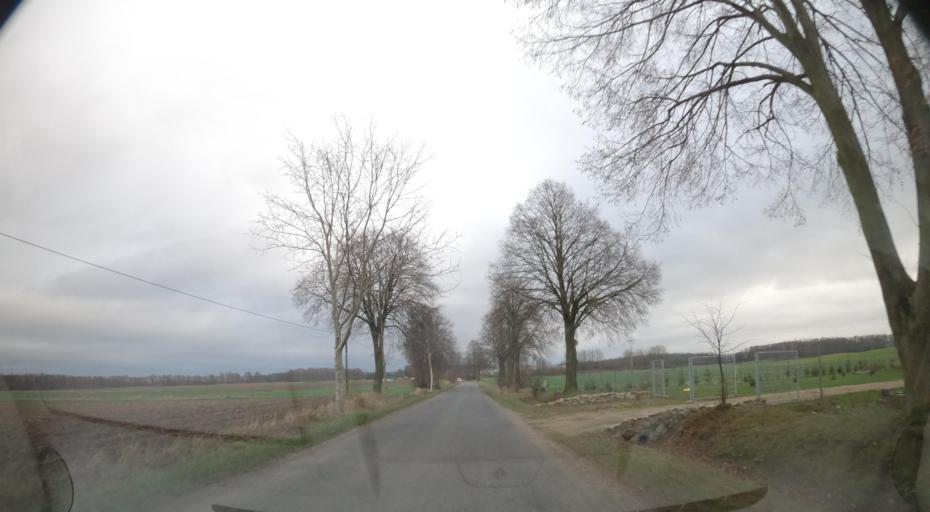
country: PL
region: Greater Poland Voivodeship
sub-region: Powiat pilski
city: Lobzenica
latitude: 53.2599
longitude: 17.1696
